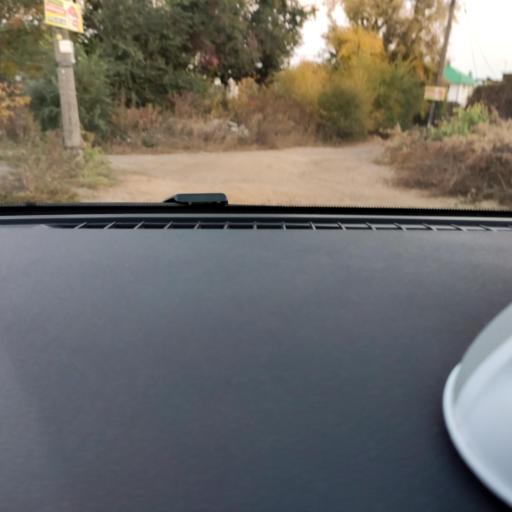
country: RU
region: Samara
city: Samara
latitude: 53.1806
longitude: 50.1994
